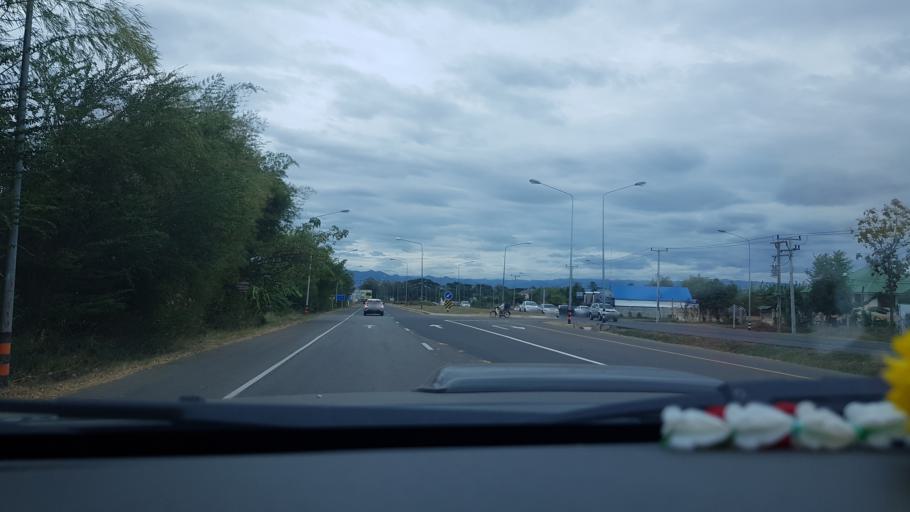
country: TH
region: Phetchabun
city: Phetchabun
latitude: 16.4973
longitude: 101.1537
